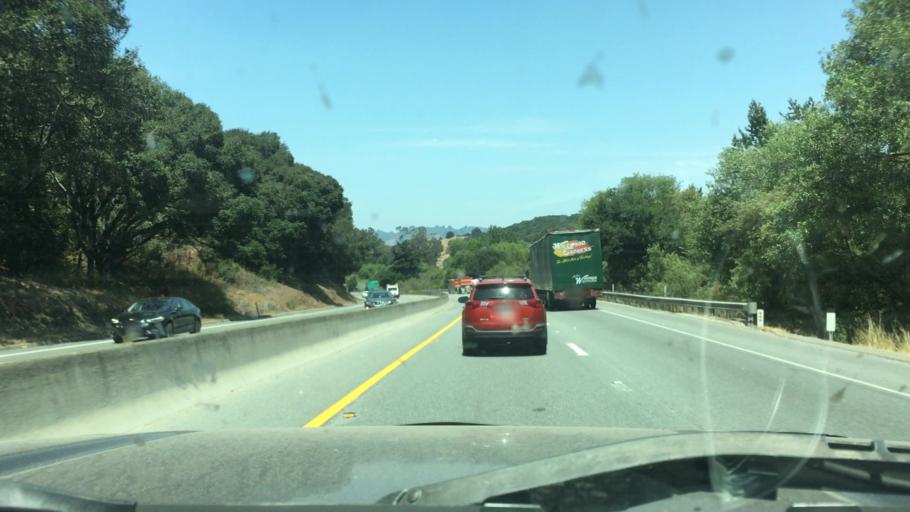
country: US
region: California
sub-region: Monterey County
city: Prunedale
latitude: 36.8250
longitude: -121.6315
